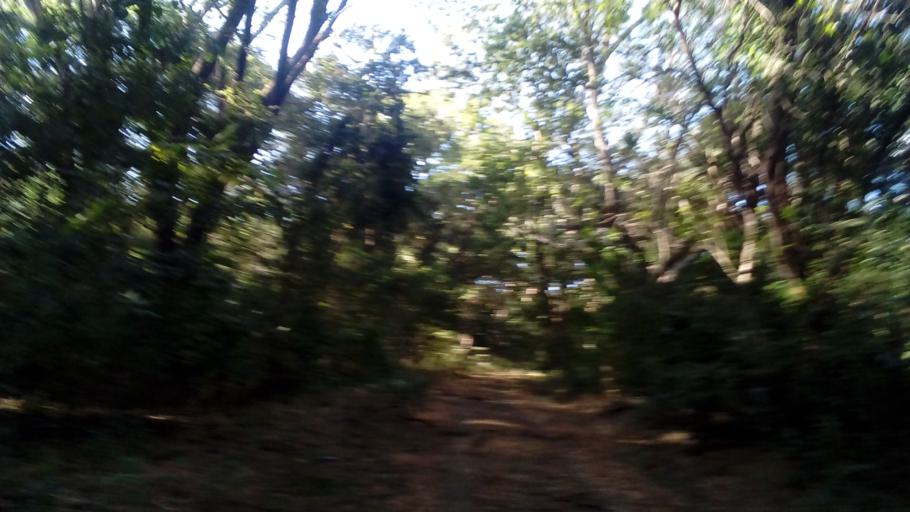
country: CR
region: Guanacaste
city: Sardinal
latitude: 10.3910
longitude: -85.8322
